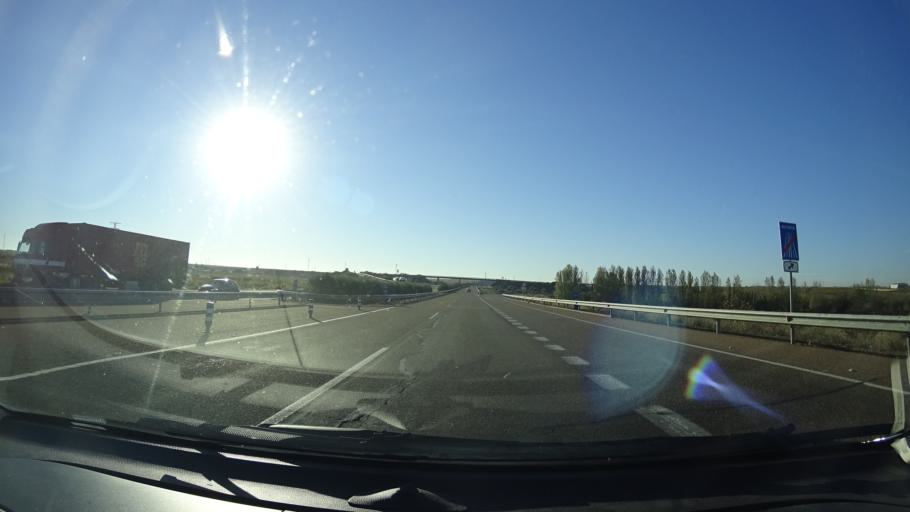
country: ES
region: Extremadura
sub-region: Provincia de Badajoz
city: Almendralejo
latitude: 38.6946
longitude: -6.3857
